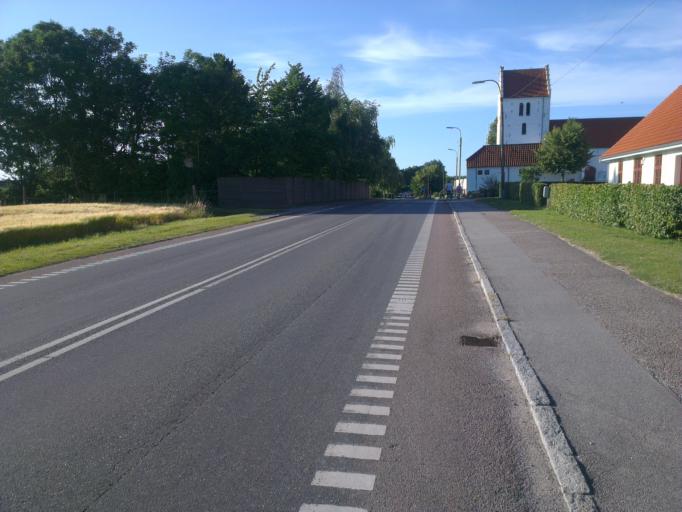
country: DK
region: Capital Region
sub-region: Frederikssund Kommune
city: Jaegerspris
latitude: 55.8196
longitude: 12.0137
